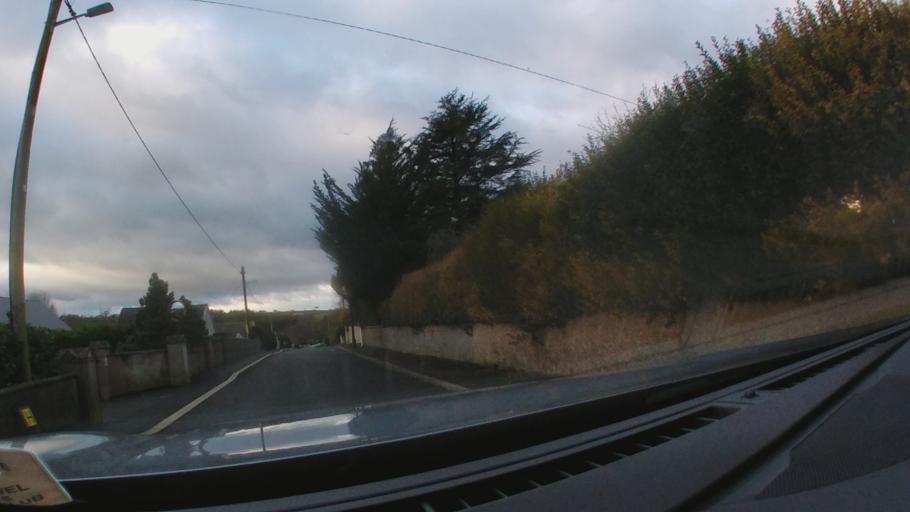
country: IE
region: Leinster
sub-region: Kilkenny
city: Thomastown
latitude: 52.5893
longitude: -7.1774
